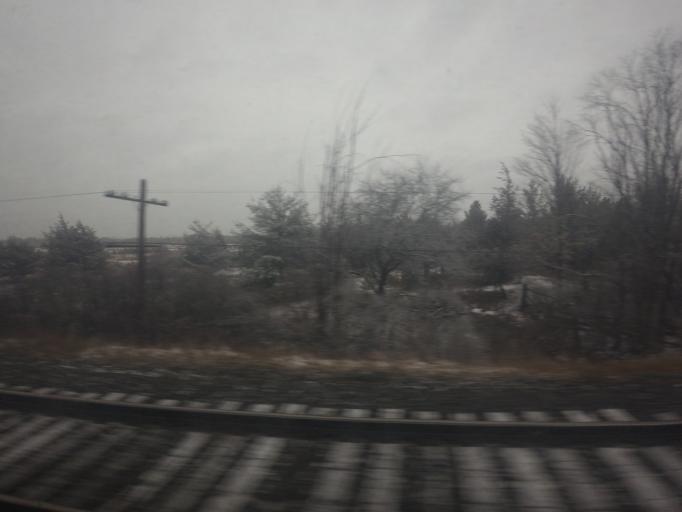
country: US
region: New York
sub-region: Jefferson County
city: Alexandria Bay
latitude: 44.4640
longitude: -75.9065
